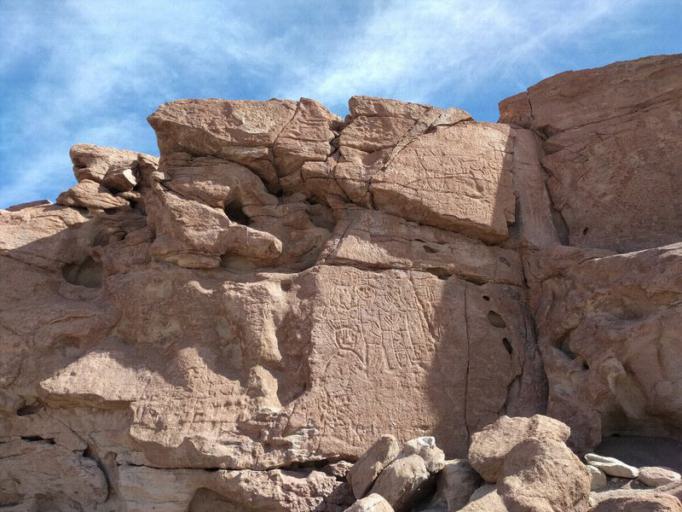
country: CL
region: Antofagasta
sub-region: Provincia de El Loa
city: San Pedro de Atacama
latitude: -22.6751
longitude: -68.2363
